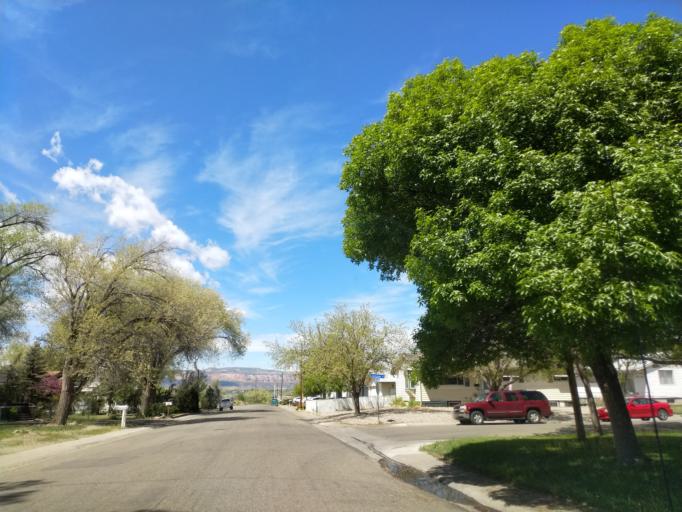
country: US
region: Colorado
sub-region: Mesa County
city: Grand Junction
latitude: 39.0792
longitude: -108.5733
